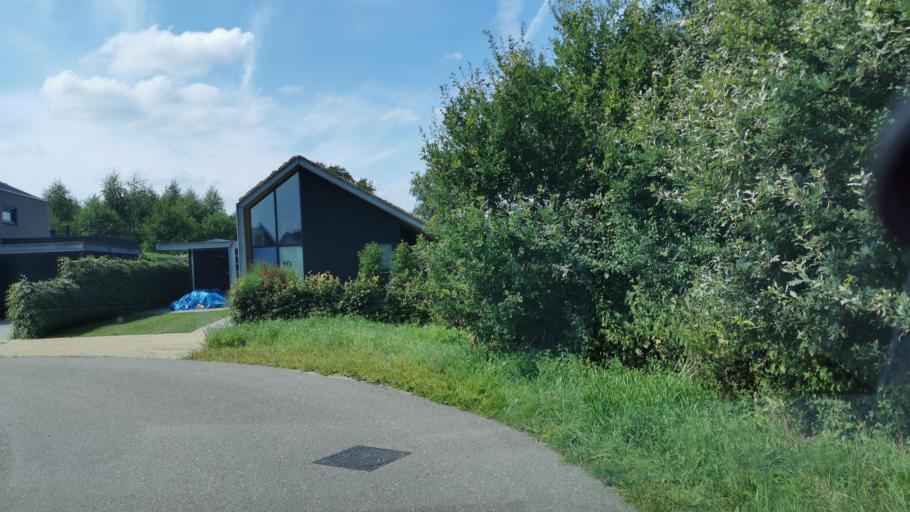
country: NL
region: Overijssel
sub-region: Gemeente Enschede
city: Enschede
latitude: 52.1838
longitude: 6.8752
